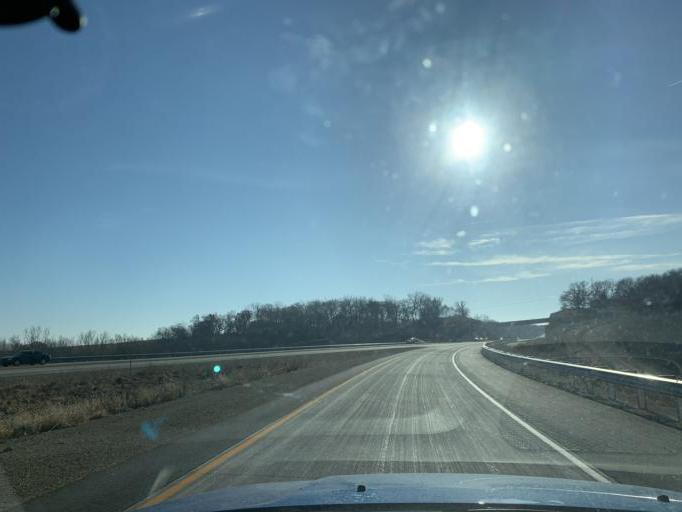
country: US
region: Wisconsin
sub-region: Iowa County
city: Dodgeville
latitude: 42.9624
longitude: -90.1049
